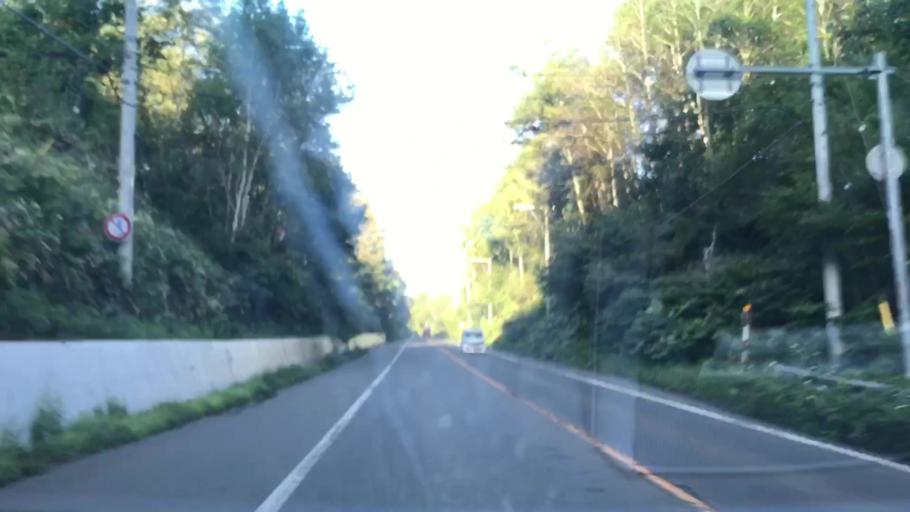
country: JP
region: Hokkaido
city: Date
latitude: 42.6099
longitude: 140.7772
